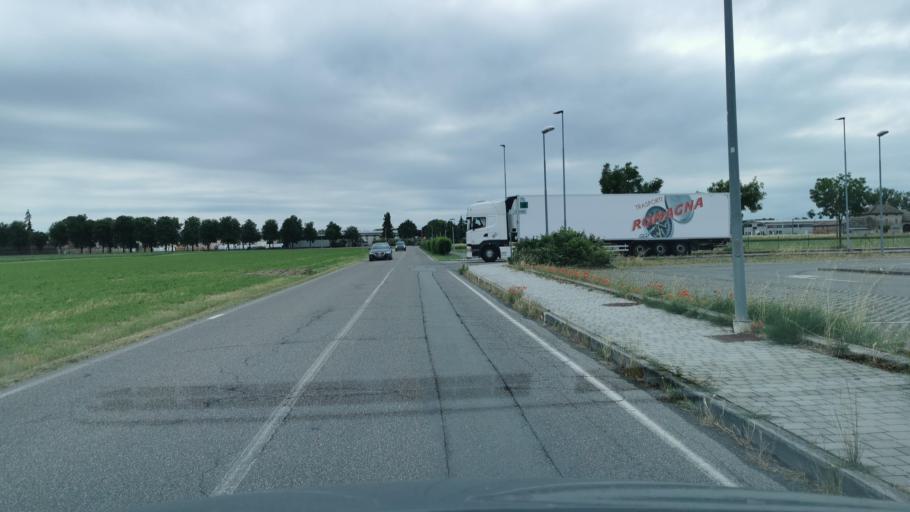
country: IT
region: Emilia-Romagna
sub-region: Provincia di Parma
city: Soragna
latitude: 44.9266
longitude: 10.1183
